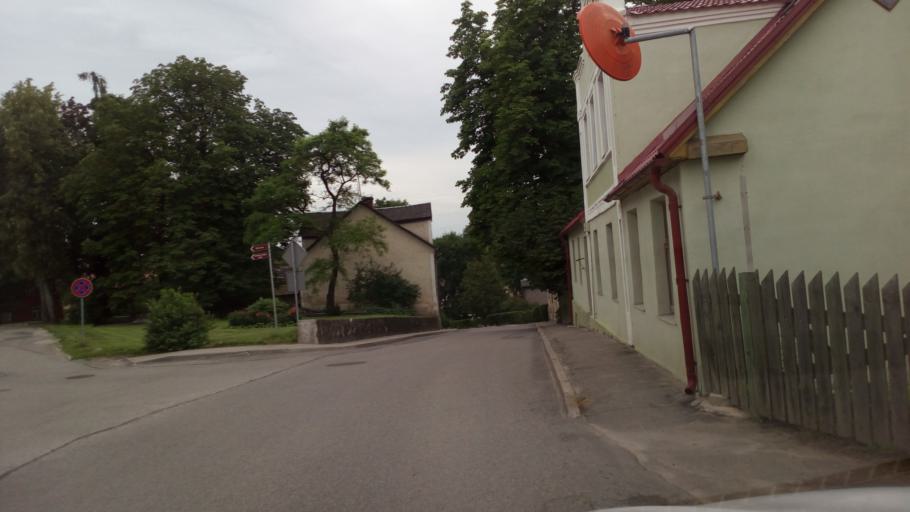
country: LV
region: Kandava
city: Kandava
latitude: 57.0388
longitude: 22.7771
